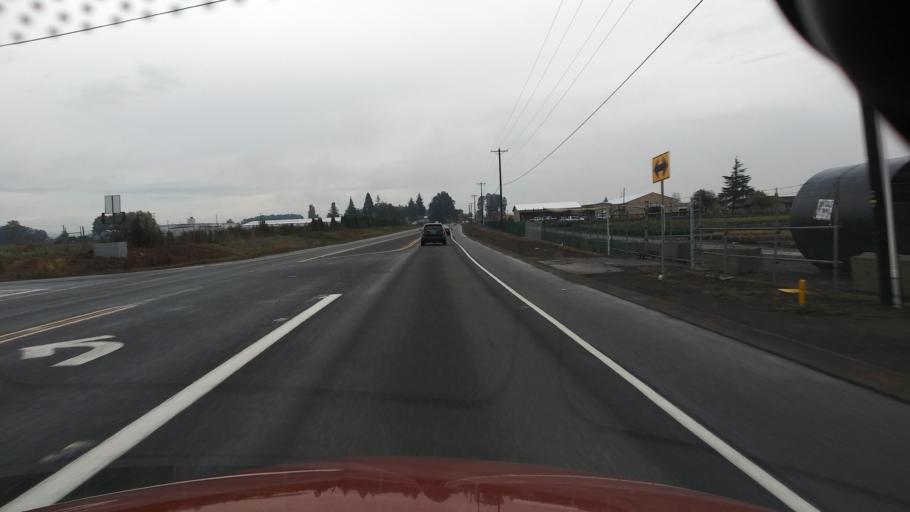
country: US
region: Oregon
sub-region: Washington County
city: Cornelius
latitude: 45.5662
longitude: -123.0513
